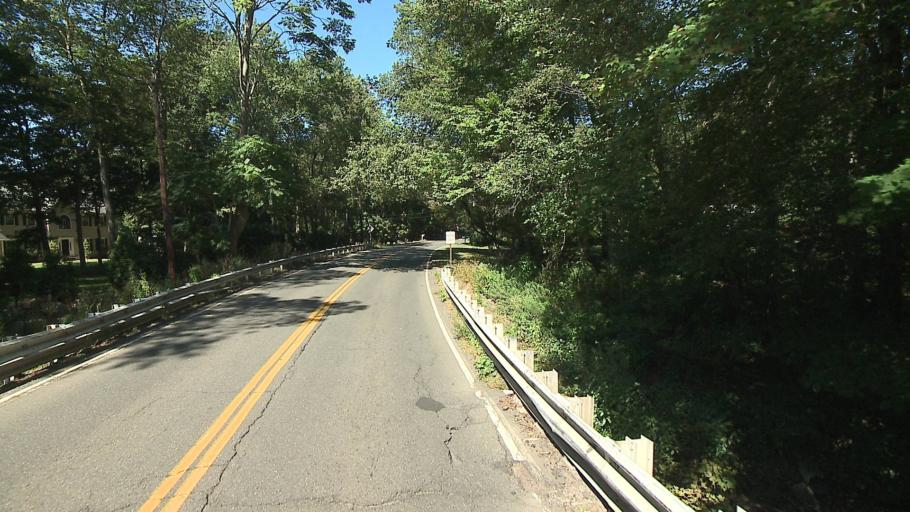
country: US
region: Connecticut
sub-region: New Haven County
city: Orange
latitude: 41.2591
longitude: -73.0514
